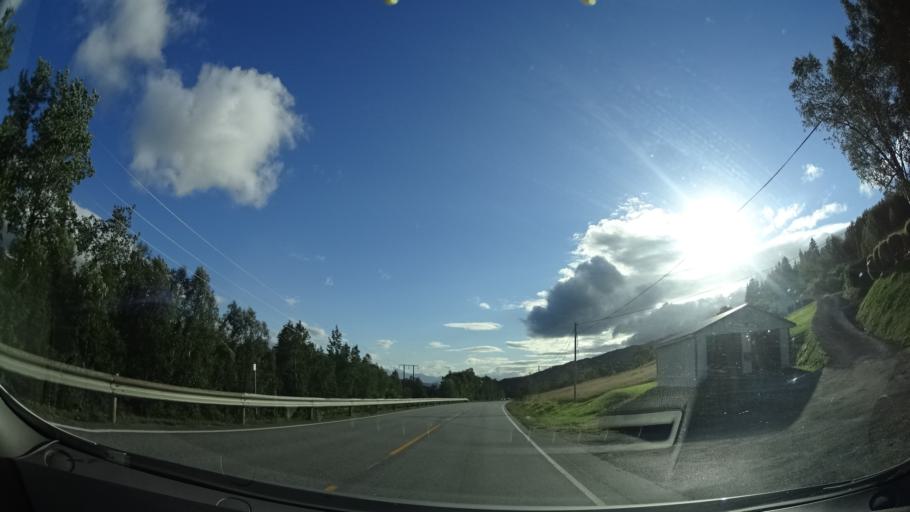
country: NO
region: More og Romsdal
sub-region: Molde
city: Hjelset
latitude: 62.8031
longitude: 7.5726
